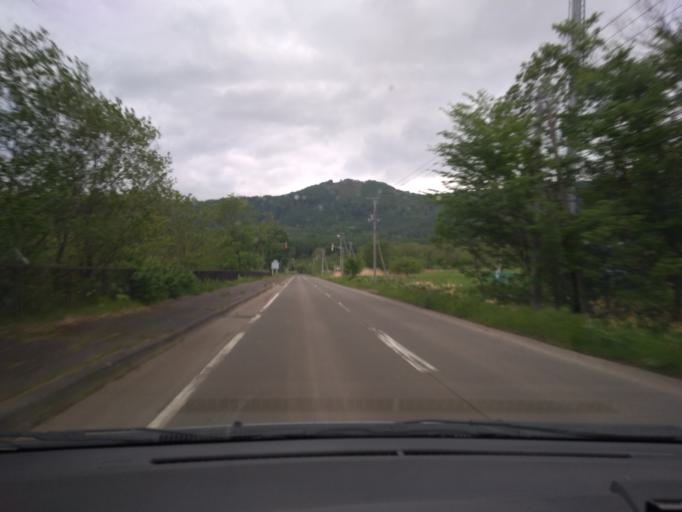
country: JP
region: Hokkaido
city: Shimo-furano
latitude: 43.1762
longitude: 142.5263
